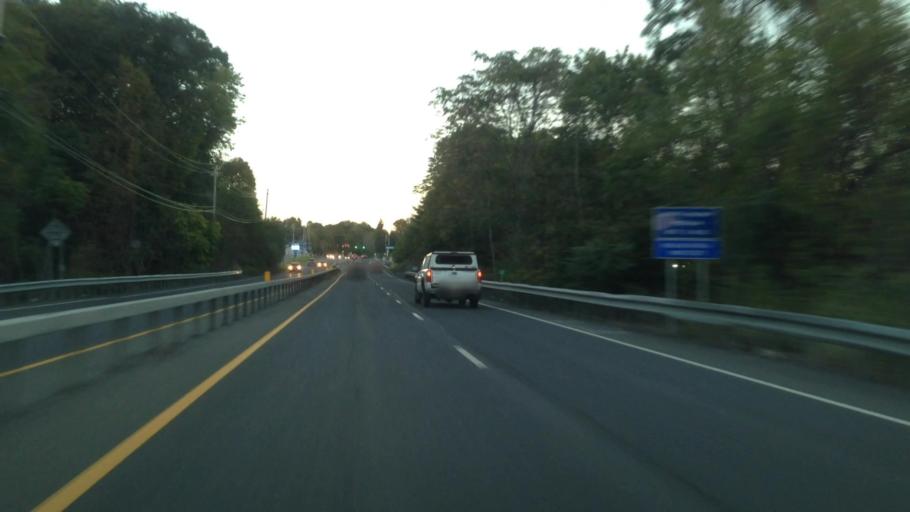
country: US
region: New York
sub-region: Ulster County
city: Highland
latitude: 41.7248
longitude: -73.9611
